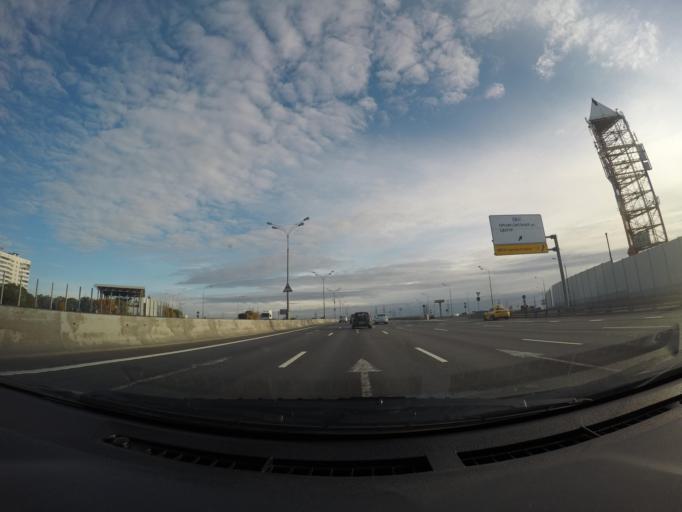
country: RU
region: Moscow
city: Tyoply Stan
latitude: 55.6133
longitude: 37.4893
